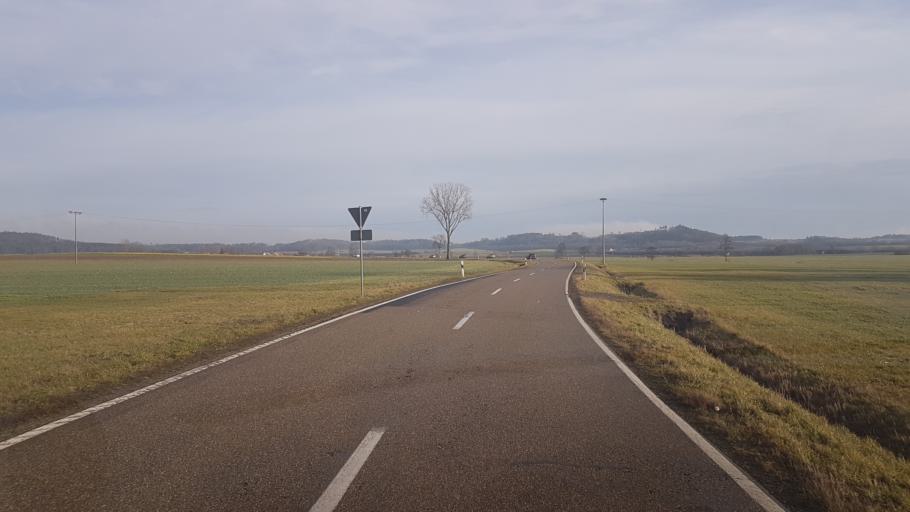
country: DE
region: Bavaria
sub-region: Regierungsbezirk Mittelfranken
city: Schnelldorf
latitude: 49.2236
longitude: 10.2289
